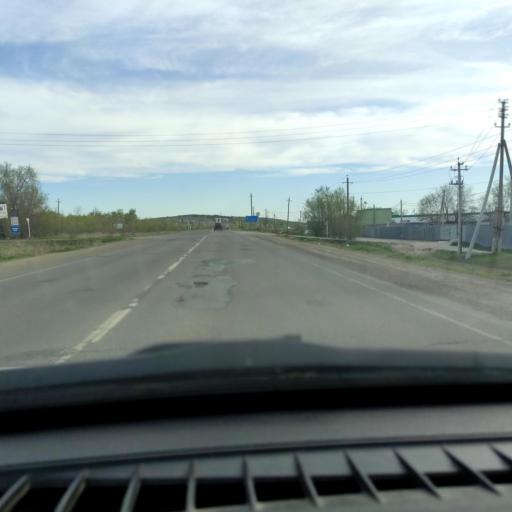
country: RU
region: Samara
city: Mirnyy
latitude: 53.4955
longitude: 50.2595
